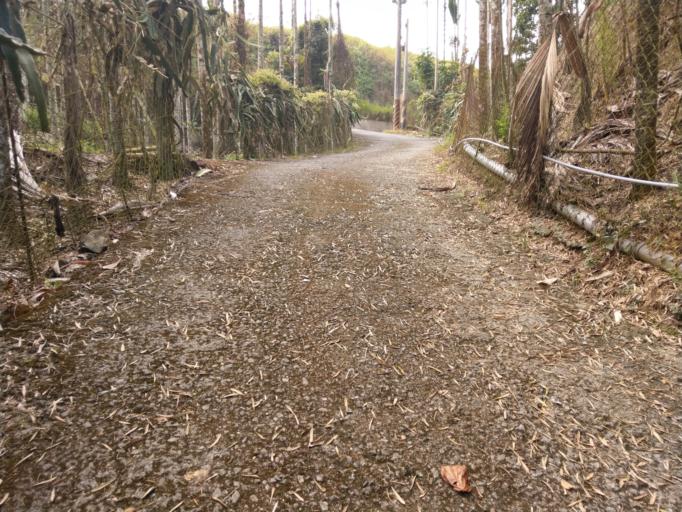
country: TW
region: Taiwan
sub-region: Nantou
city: Puli
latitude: 23.9187
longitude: 120.9223
